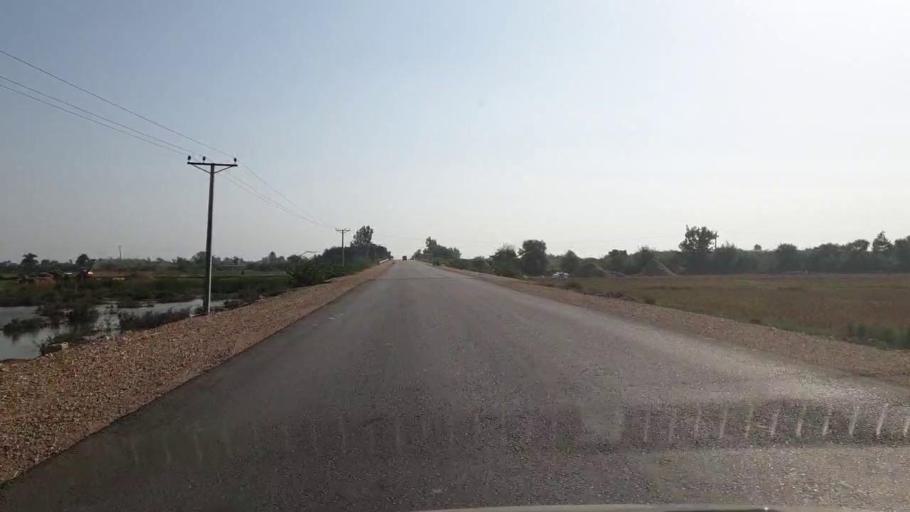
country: PK
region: Sindh
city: Tando Bago
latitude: 24.6580
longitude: 68.9699
